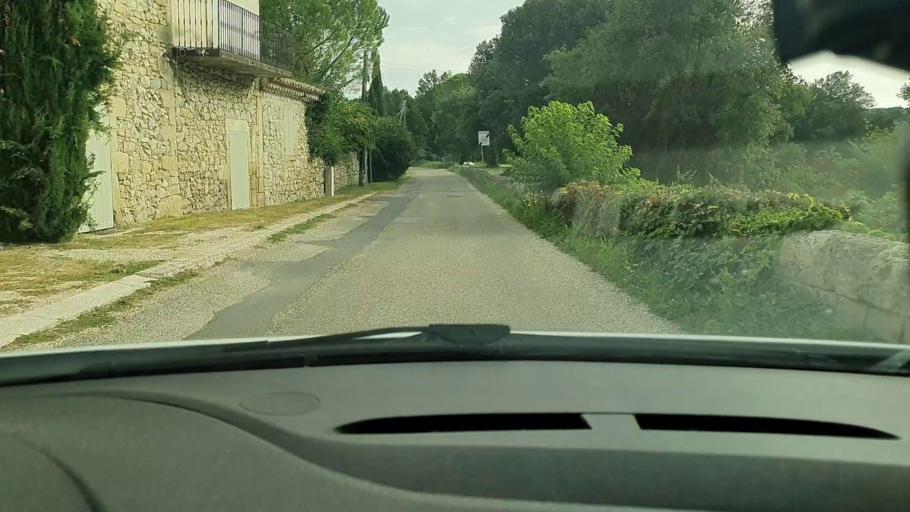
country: FR
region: Languedoc-Roussillon
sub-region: Departement du Gard
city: Montaren-et-Saint-Mediers
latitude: 44.0838
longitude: 4.3668
